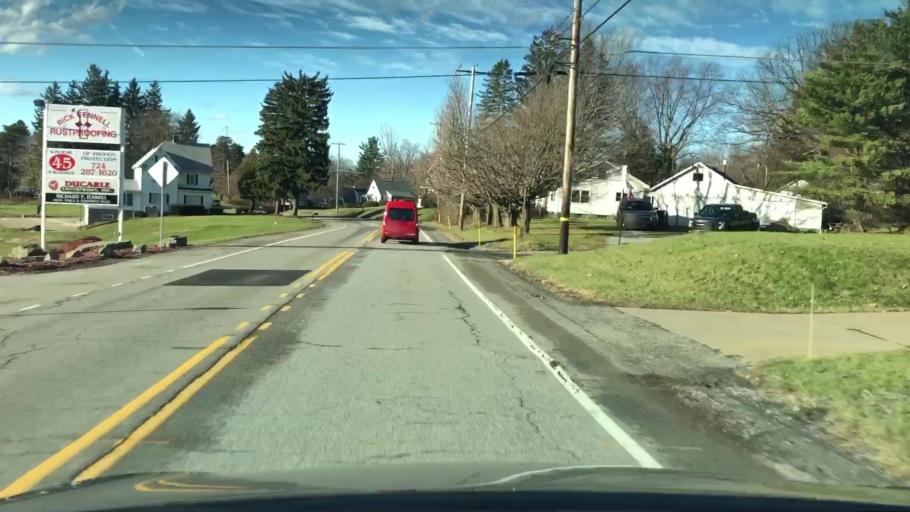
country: US
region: Pennsylvania
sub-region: Butler County
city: Meadowood
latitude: 40.8393
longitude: -79.8691
